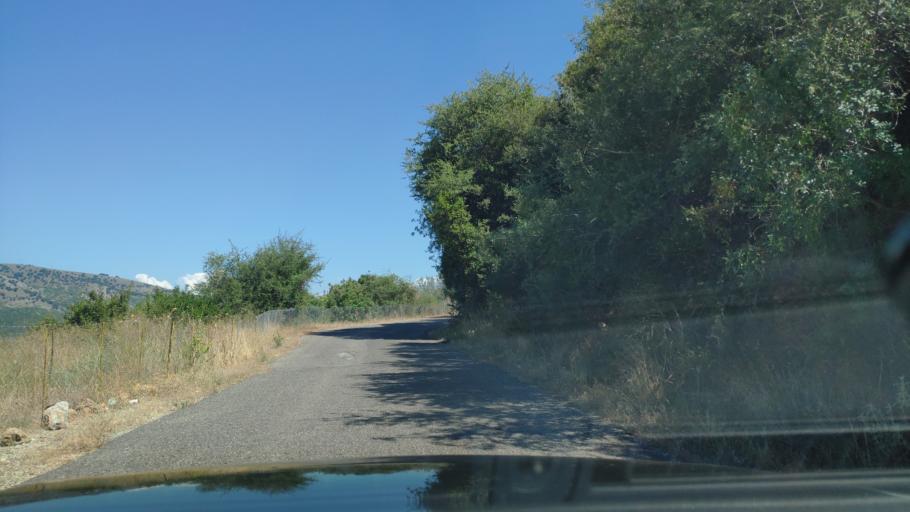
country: GR
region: West Greece
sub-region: Nomos Aitolias kai Akarnanias
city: Katouna
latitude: 38.8028
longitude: 21.1107
